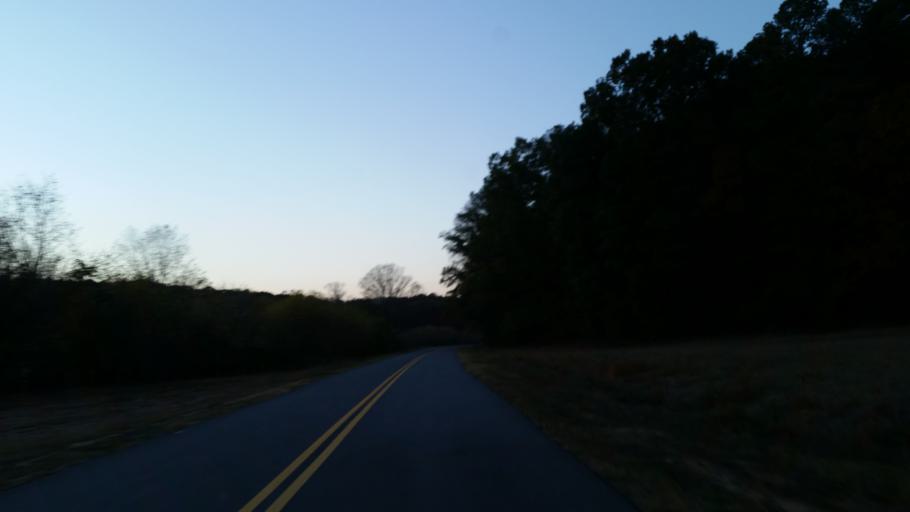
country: US
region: Georgia
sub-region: Gordon County
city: Calhoun
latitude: 34.5877
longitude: -84.9574
